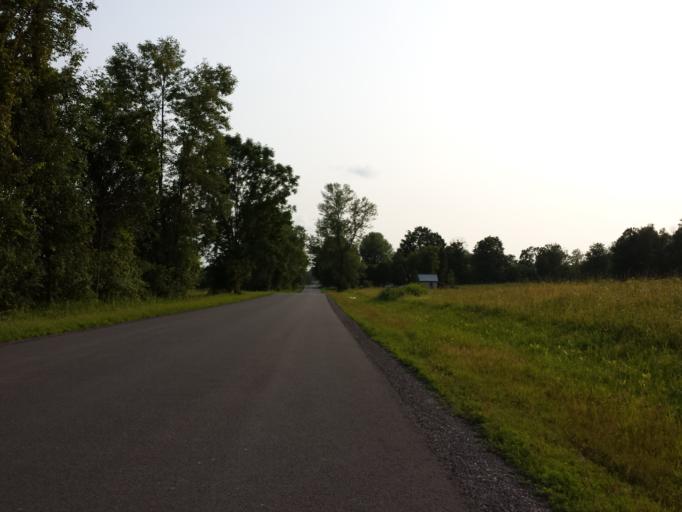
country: US
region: New York
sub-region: St. Lawrence County
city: Potsdam
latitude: 44.7000
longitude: -74.9165
